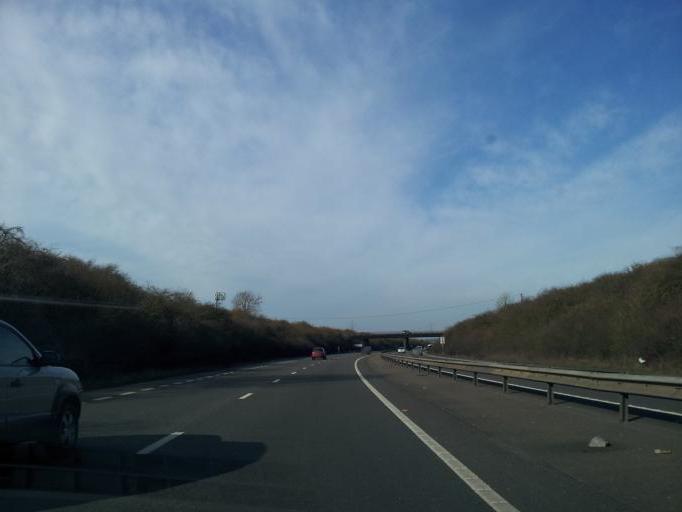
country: GB
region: England
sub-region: Lincolnshire
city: Long Bennington
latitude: 52.9907
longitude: -0.7634
